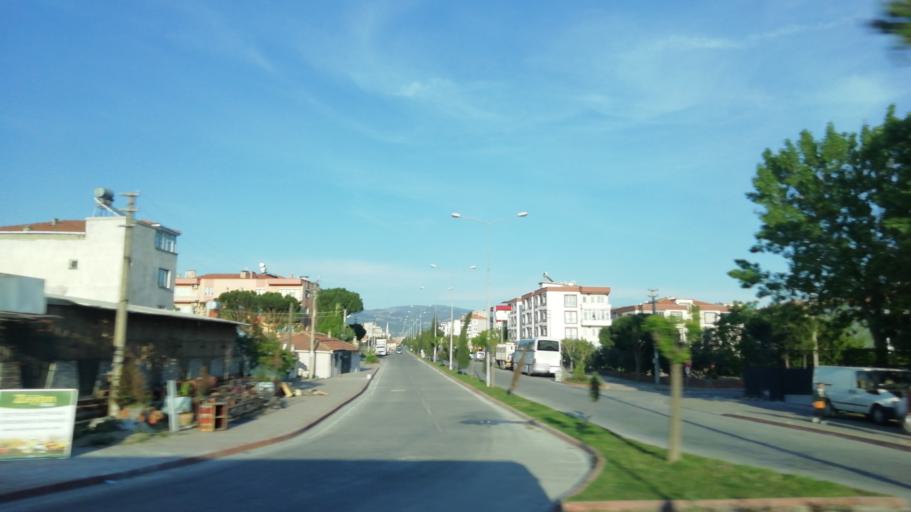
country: TR
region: Manisa
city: Akhisar
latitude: 38.9316
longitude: 27.8347
